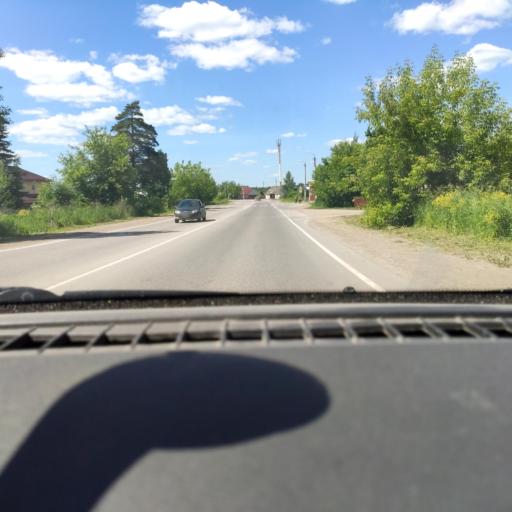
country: RU
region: Perm
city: Ust'-Kachka
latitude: 58.0762
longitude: 55.6733
